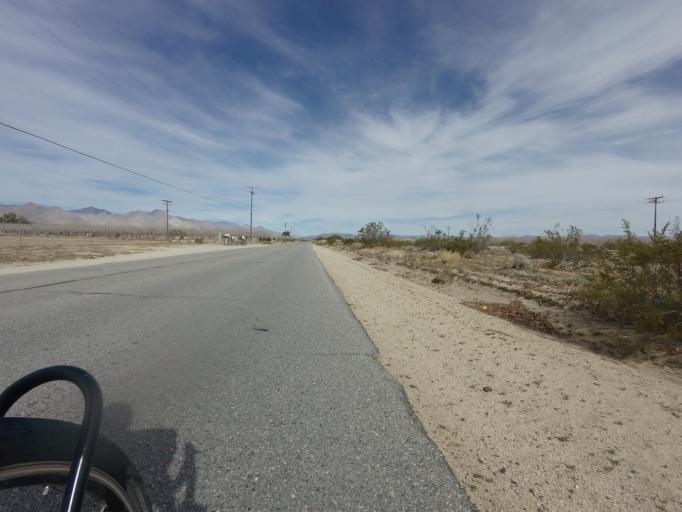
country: US
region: California
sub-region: Kern County
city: Inyokern
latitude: 35.7028
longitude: -117.8289
